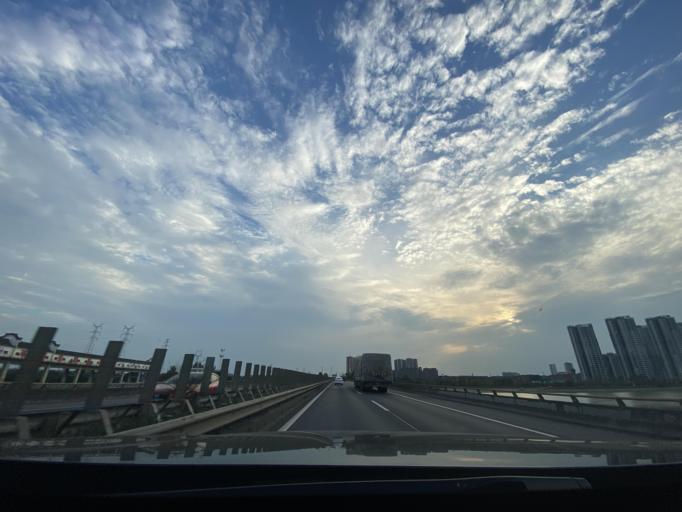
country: CN
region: Sichuan
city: Deyang
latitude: 31.0832
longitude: 104.3980
